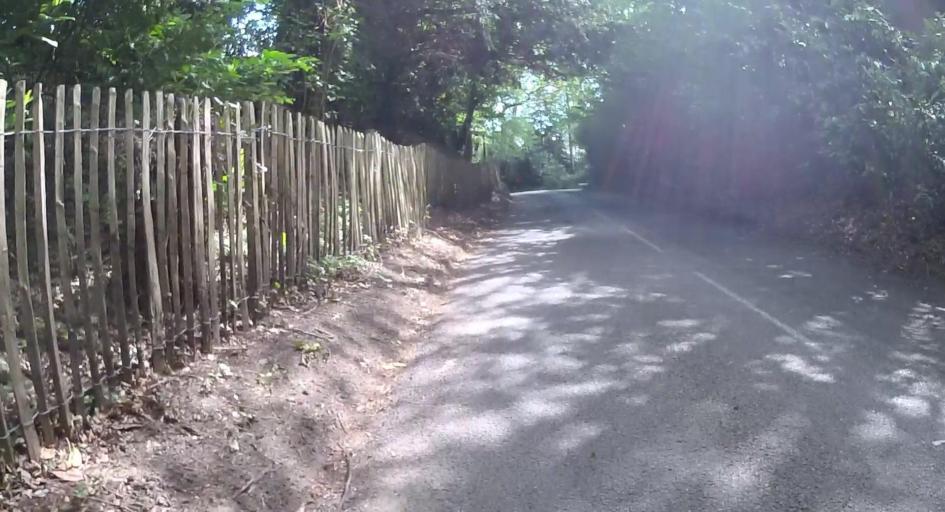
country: GB
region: England
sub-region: Surrey
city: Farnham
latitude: 51.1881
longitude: -0.7851
